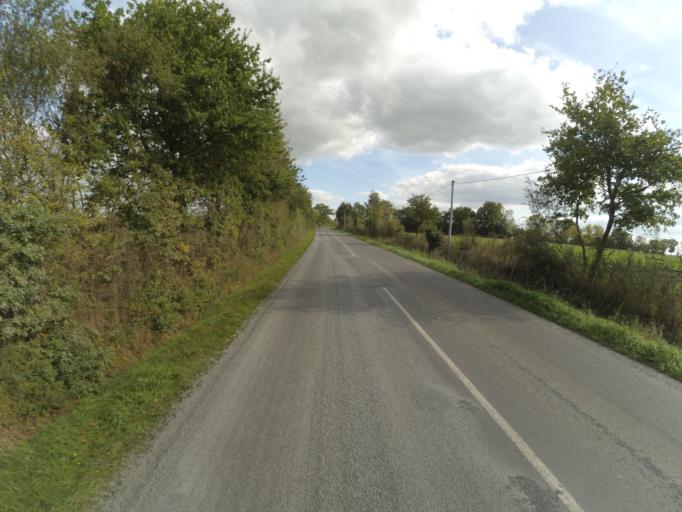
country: FR
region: Pays de la Loire
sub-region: Departement de la Loire-Atlantique
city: Casson
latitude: 47.4086
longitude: -1.5963
